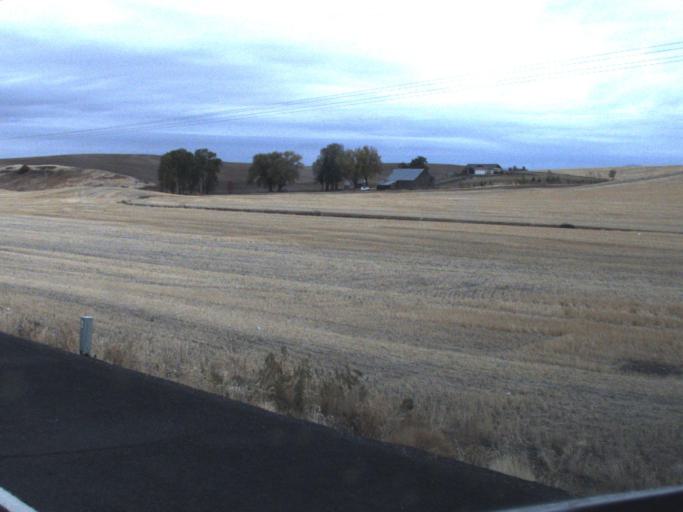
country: US
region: Washington
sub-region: Whitman County
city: Pullman
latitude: 46.6941
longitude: -117.2041
